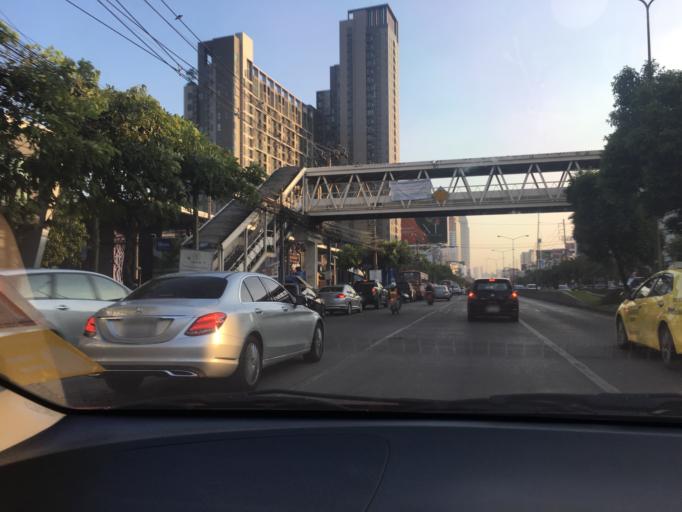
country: TH
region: Bangkok
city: Huai Khwang
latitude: 13.7823
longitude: 100.5738
